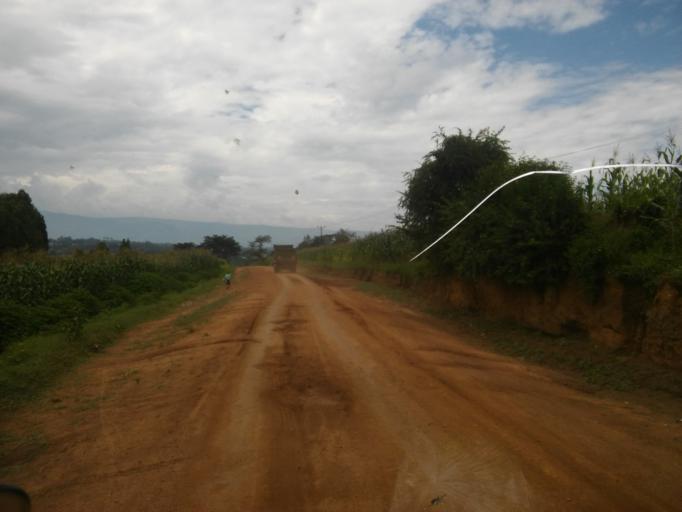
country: KE
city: Malikisi
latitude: 0.8121
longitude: 34.3385
